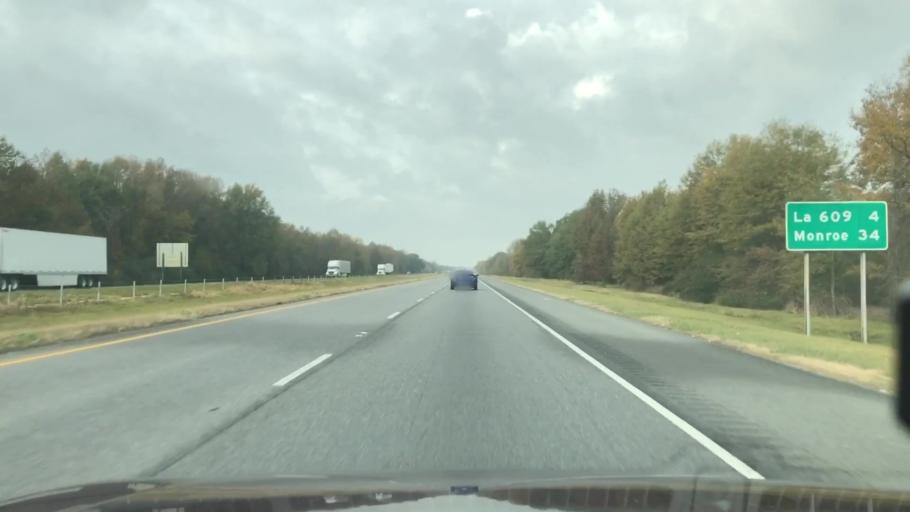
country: US
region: Louisiana
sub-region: Richland Parish
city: Delhi
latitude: 32.4451
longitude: -91.5093
